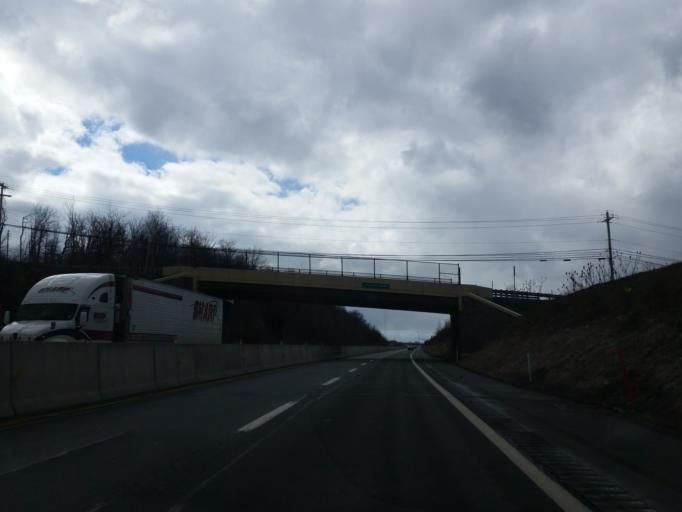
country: US
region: Pennsylvania
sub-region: Luzerne County
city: Dupont
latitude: 41.3159
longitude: -75.7433
